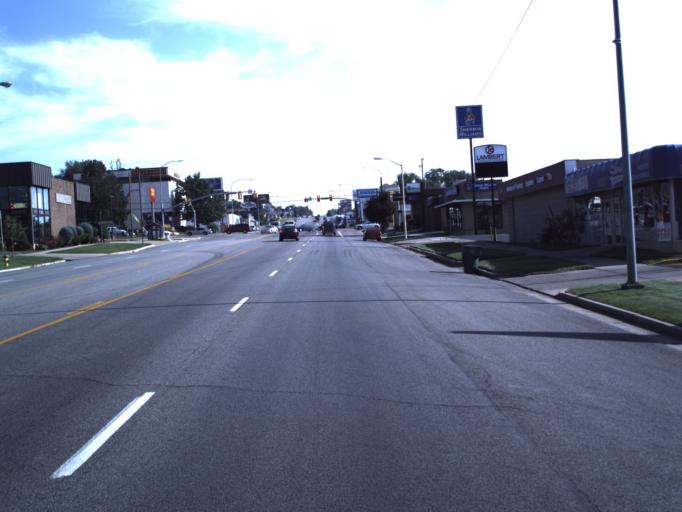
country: US
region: Utah
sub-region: Weber County
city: South Ogden
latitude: 41.1993
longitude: -111.9711
